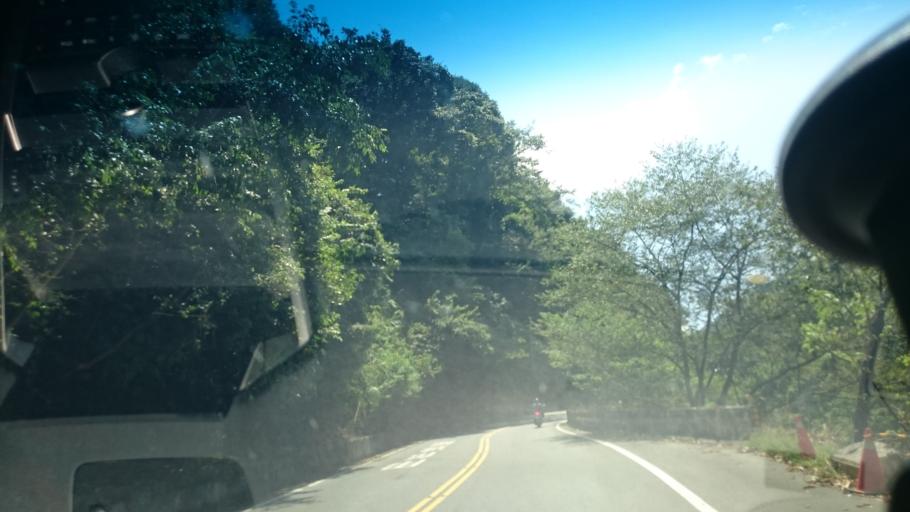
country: TW
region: Taiwan
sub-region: Nantou
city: Puli
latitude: 24.0153
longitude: 121.1238
